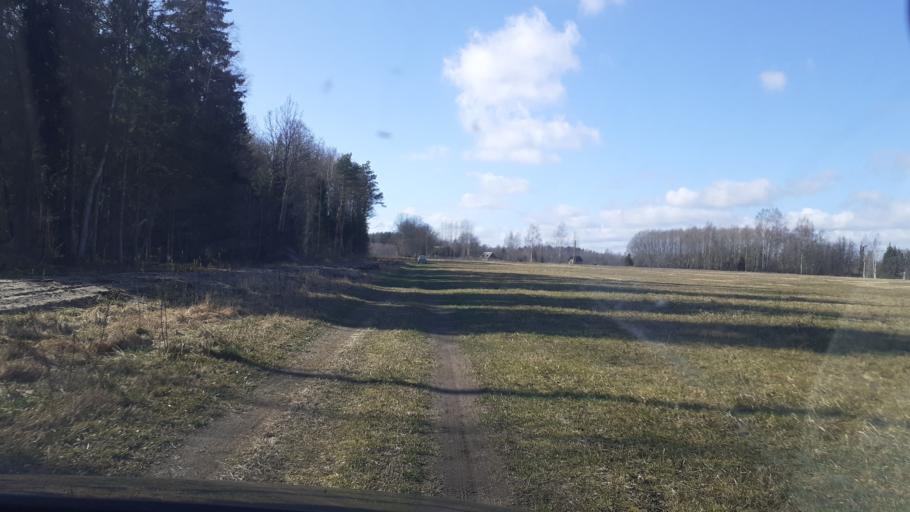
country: LV
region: Kuldigas Rajons
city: Kuldiga
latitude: 56.8758
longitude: 22.1127
